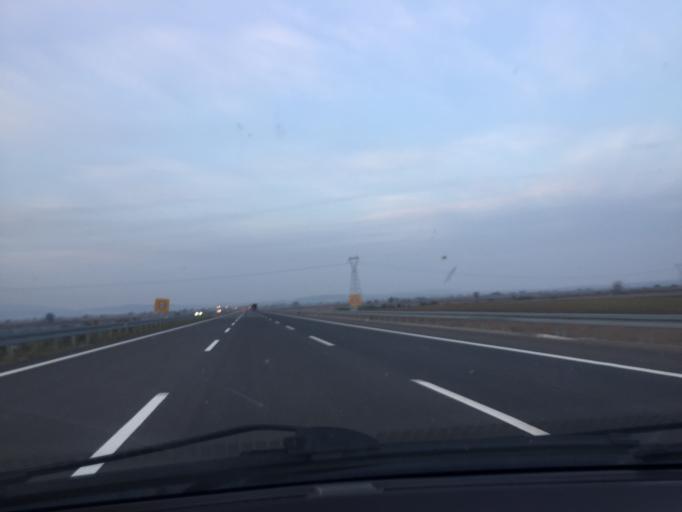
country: TR
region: Manisa
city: Halitpasa
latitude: 38.7153
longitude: 27.6493
